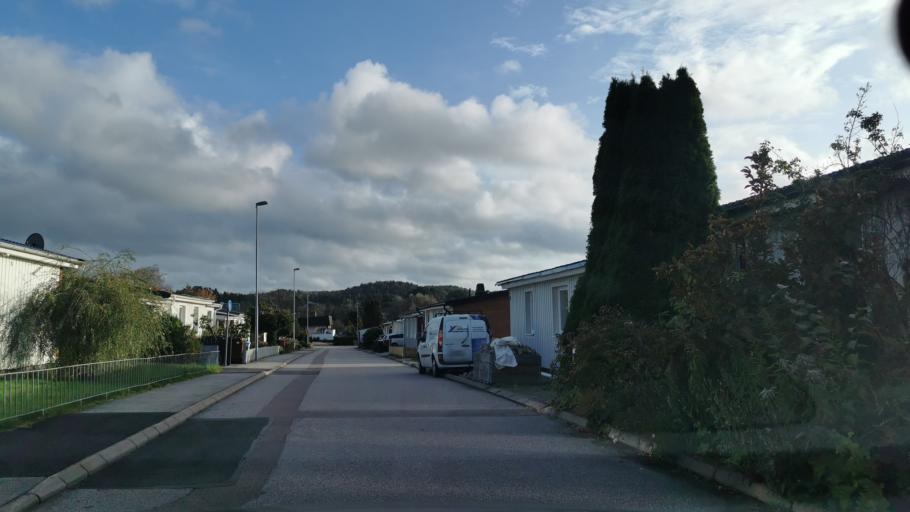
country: SE
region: Vaestra Goetaland
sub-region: Partille Kommun
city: Partille
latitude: 57.7246
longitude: 12.0765
